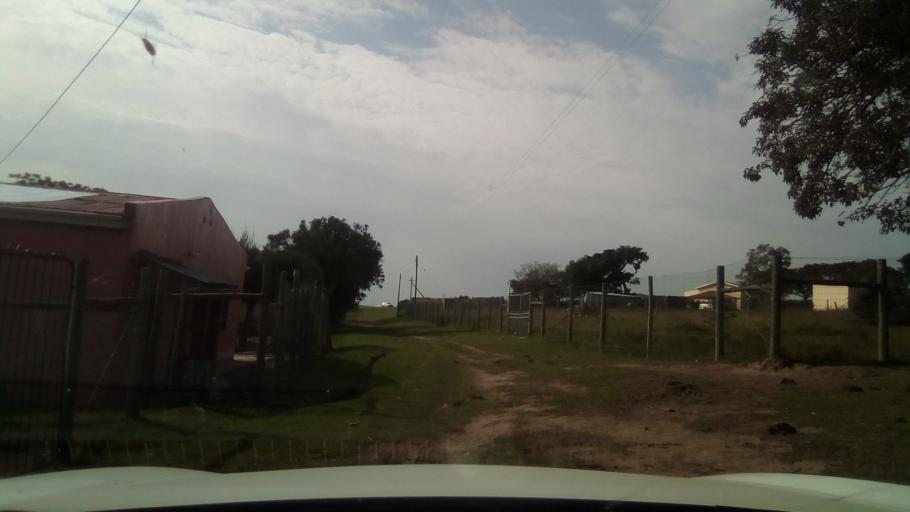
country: ZA
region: Eastern Cape
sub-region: Buffalo City Metropolitan Municipality
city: Bhisho
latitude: -33.0052
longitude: 27.2995
